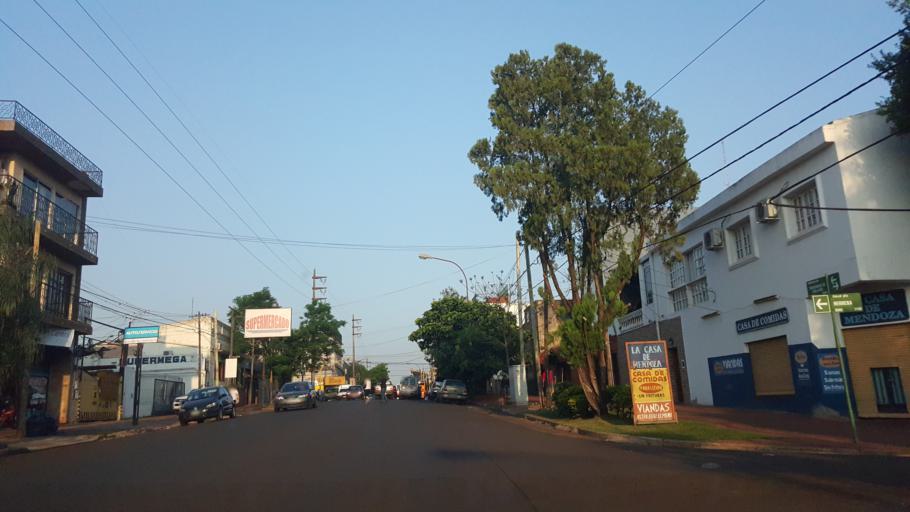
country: AR
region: Misiones
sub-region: Departamento de Capital
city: Posadas
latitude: -27.3775
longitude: -55.9003
